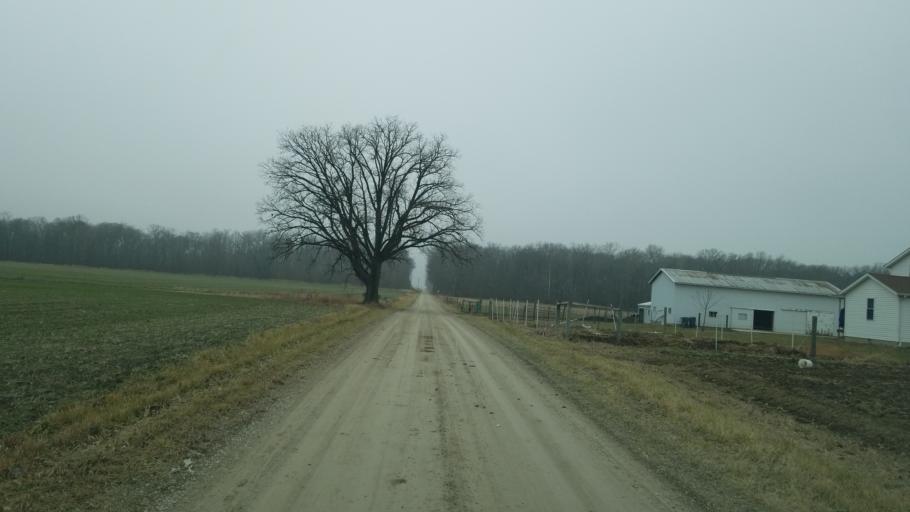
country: US
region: Indiana
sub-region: Adams County
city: Geneva
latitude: 40.5838
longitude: -85.0049
